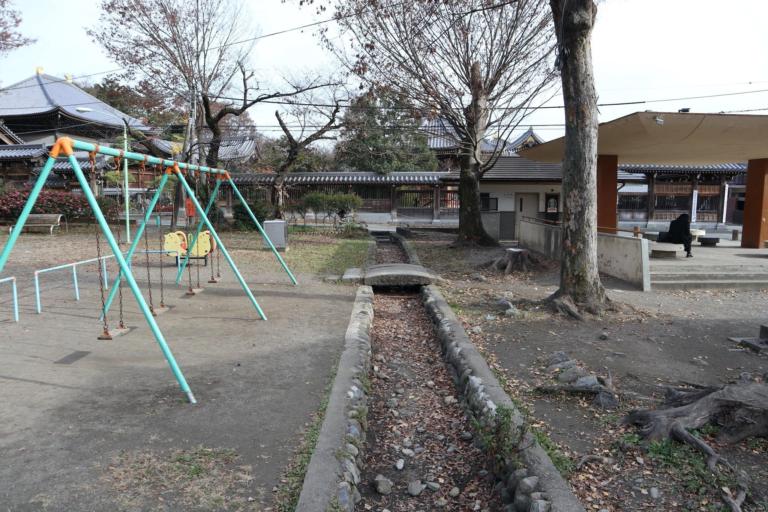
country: JP
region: Tokyo
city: Fussa
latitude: 35.7054
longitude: 139.3462
